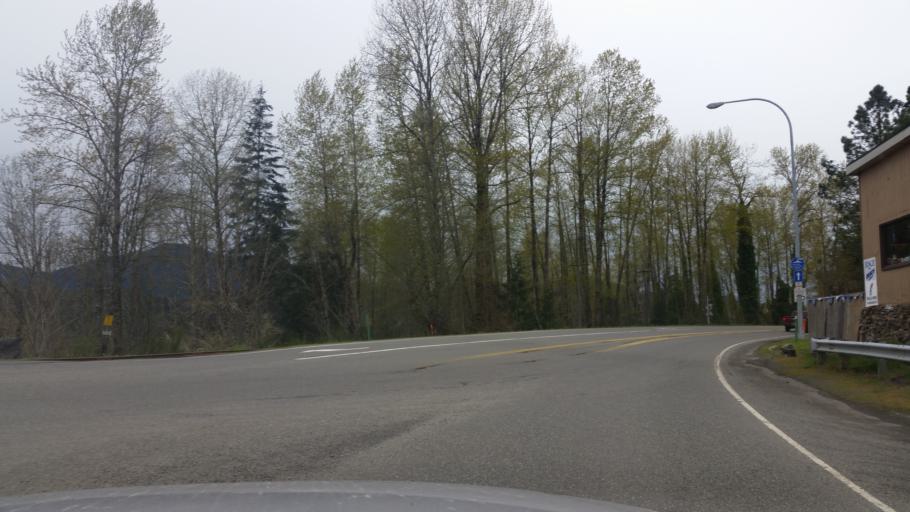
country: US
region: Washington
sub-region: Pierce County
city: Eatonville
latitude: 46.7632
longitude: -122.1919
